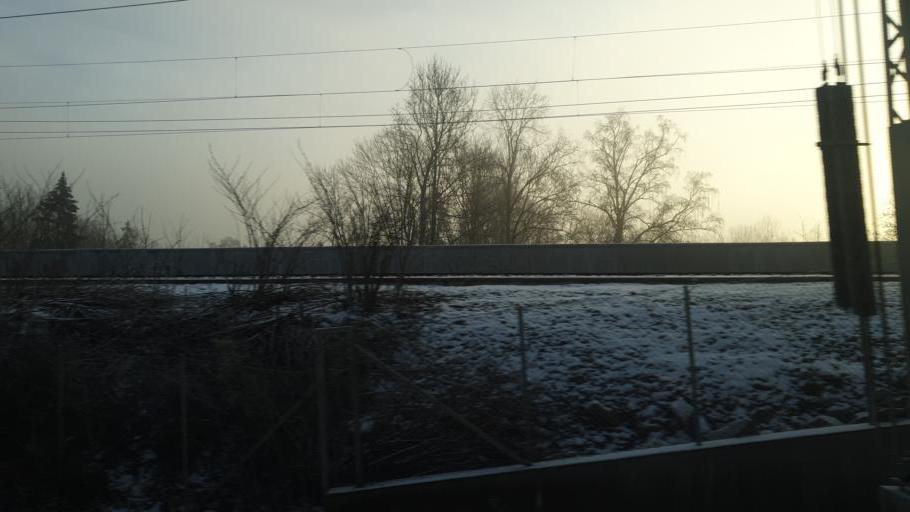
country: NO
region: Akershus
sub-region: Asker
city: Billingstad
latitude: 59.8855
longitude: 10.4977
